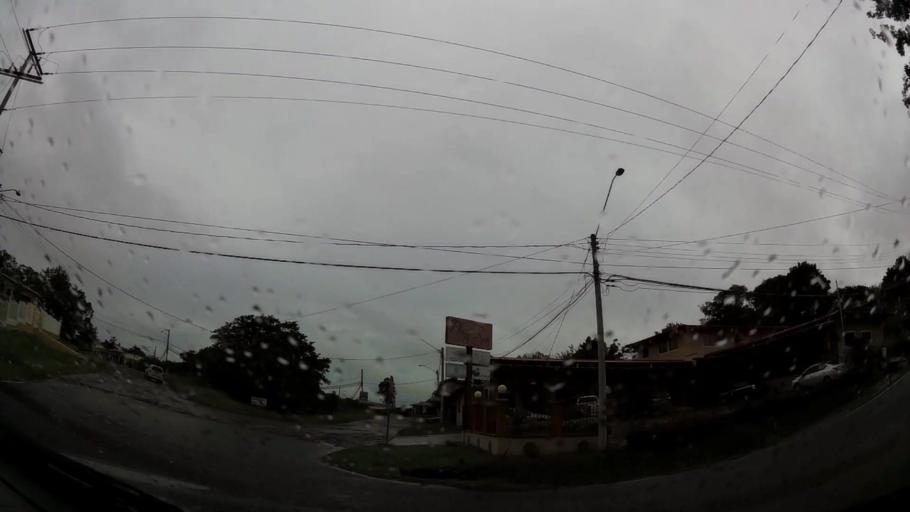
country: PA
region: Veraguas
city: Santiago de Veraguas
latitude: 8.0919
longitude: -80.9565
